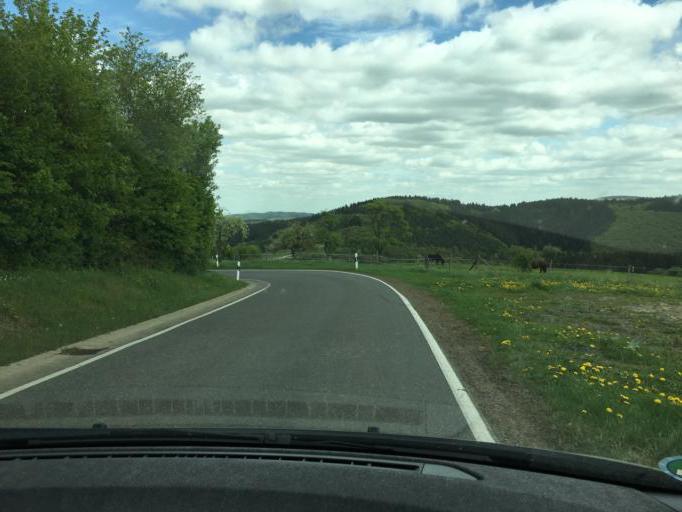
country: DE
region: Rheinland-Pfalz
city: Lind
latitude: 50.4961
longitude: 6.9421
